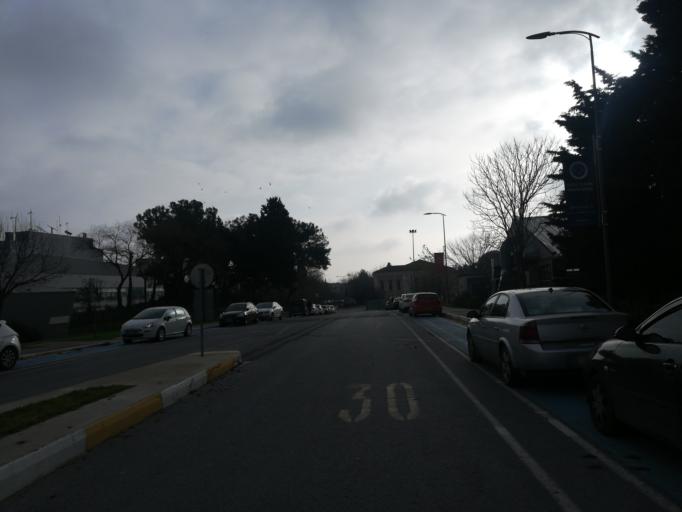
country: TR
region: Istanbul
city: merter keresteciler
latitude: 41.0284
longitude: 28.8887
